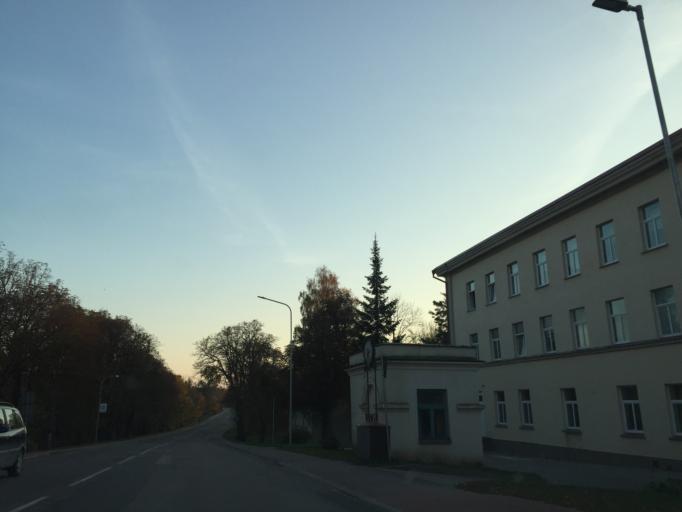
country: LV
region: Priekule
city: Priekule
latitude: 56.4420
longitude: 21.5844
